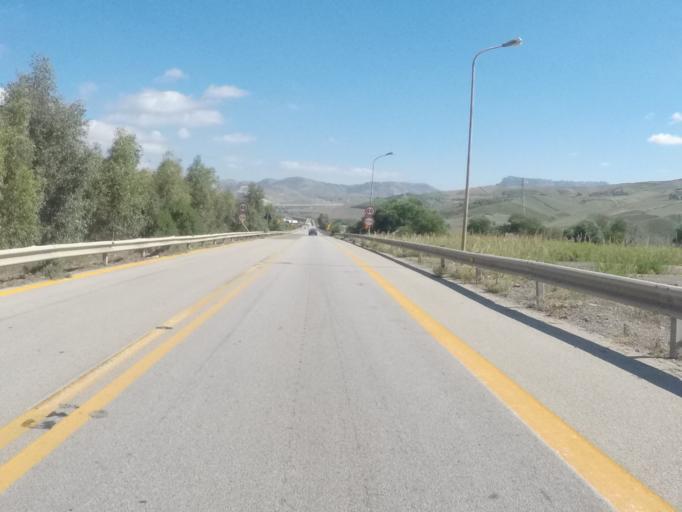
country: IT
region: Sicily
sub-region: Enna
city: Villarosa
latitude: 37.5415
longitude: 14.1700
